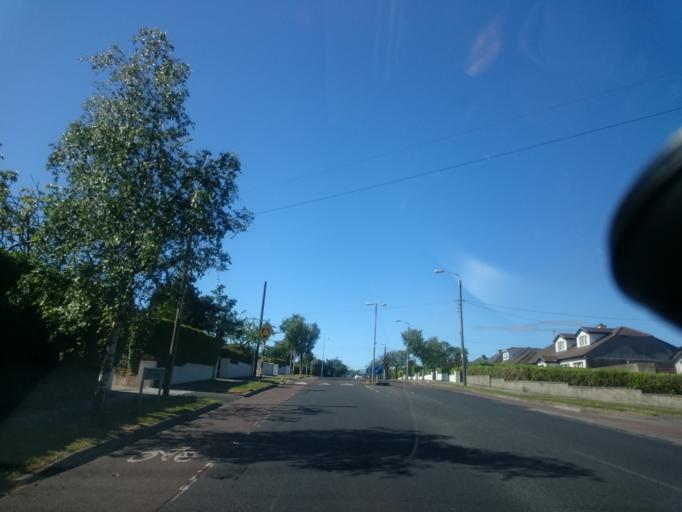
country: IE
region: Leinster
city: Sallynoggin
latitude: 53.2743
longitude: -6.1234
